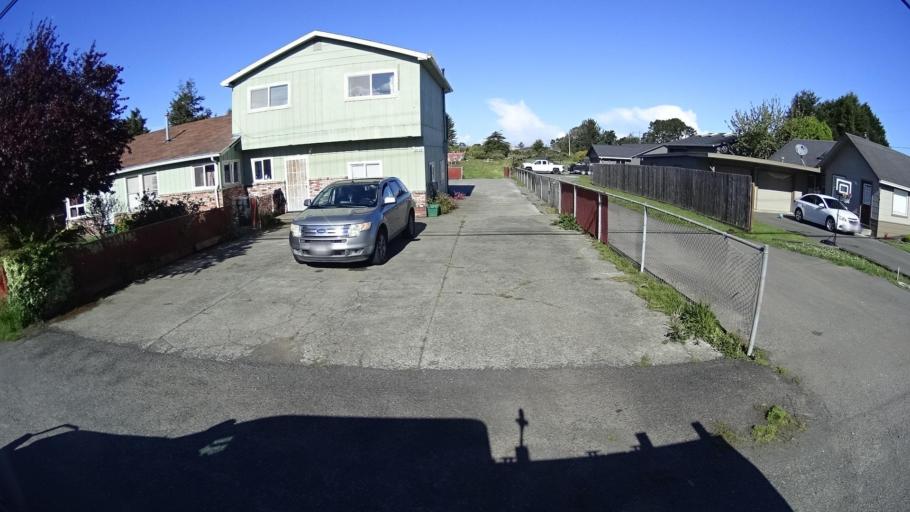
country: US
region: California
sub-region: Humboldt County
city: McKinleyville
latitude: 40.9710
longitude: -124.0959
